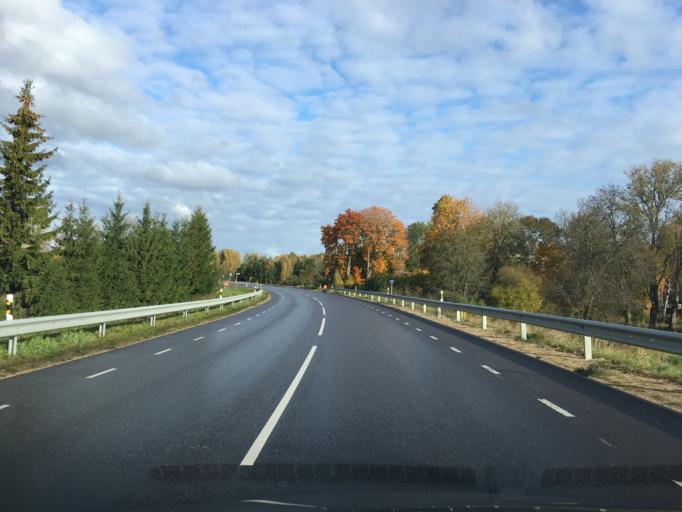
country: EE
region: Harju
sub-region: Raasiku vald
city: Raasiku
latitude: 59.1930
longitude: 25.1852
